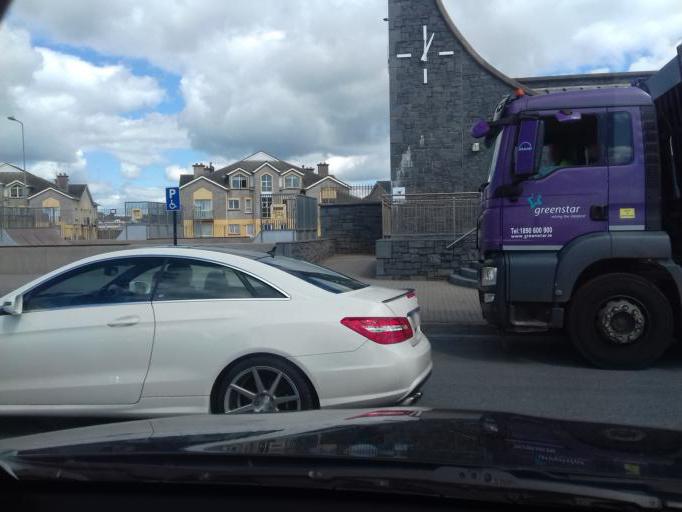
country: IE
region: Munster
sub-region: Waterford
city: Tra Mhor
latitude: 52.1594
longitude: -7.1383
